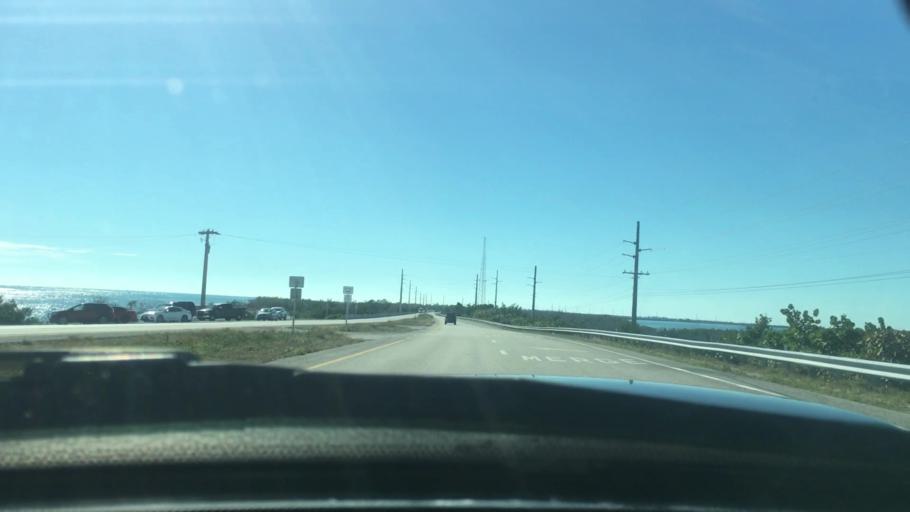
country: US
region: Florida
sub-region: Monroe County
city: Big Pine Key
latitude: 24.6557
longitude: -81.2987
